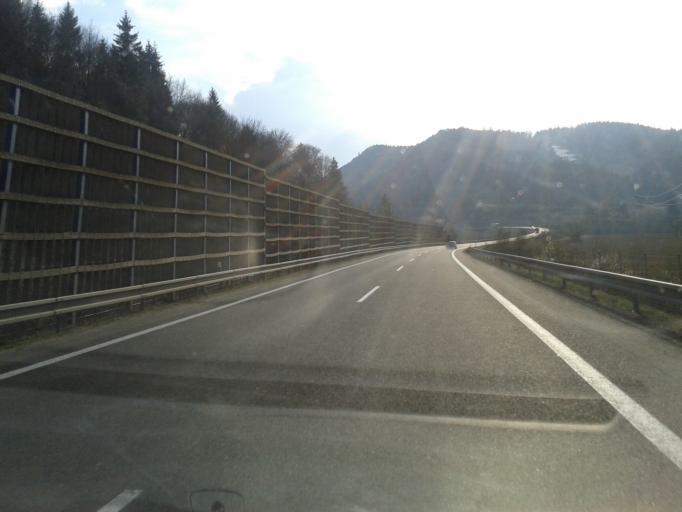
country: SK
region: Zilinsky
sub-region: Okres Dolny Kubin
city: Dolny Kubin
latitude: 49.2555
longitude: 19.3513
